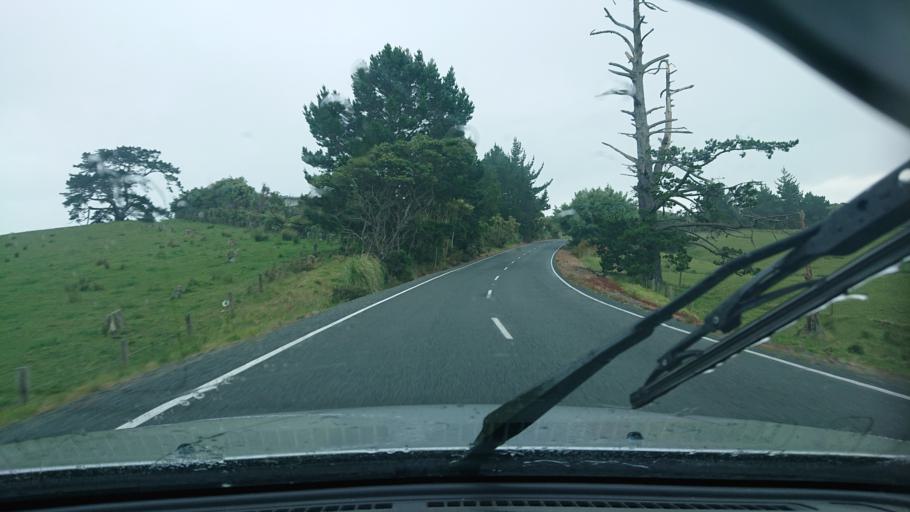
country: NZ
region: Auckland
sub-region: Auckland
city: Wellsford
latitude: -36.3329
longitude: 174.4009
